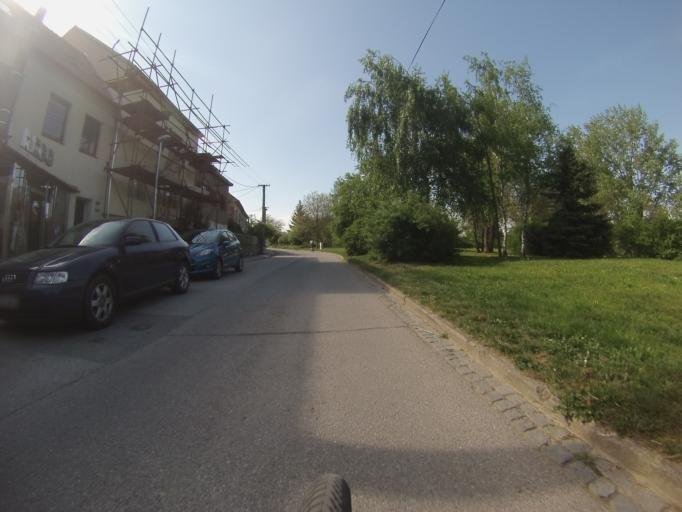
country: CZ
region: South Moravian
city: Troubsko
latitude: 49.2230
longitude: 16.5339
